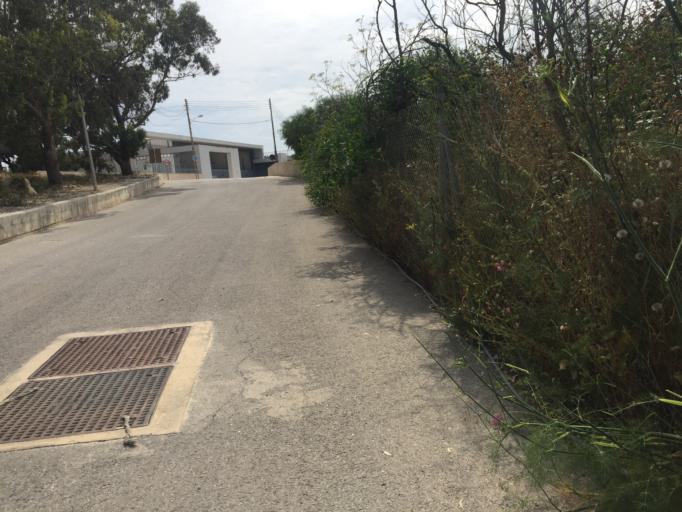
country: MT
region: Tas-Sliema
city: Sliema
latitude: 35.9048
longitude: 14.5039
